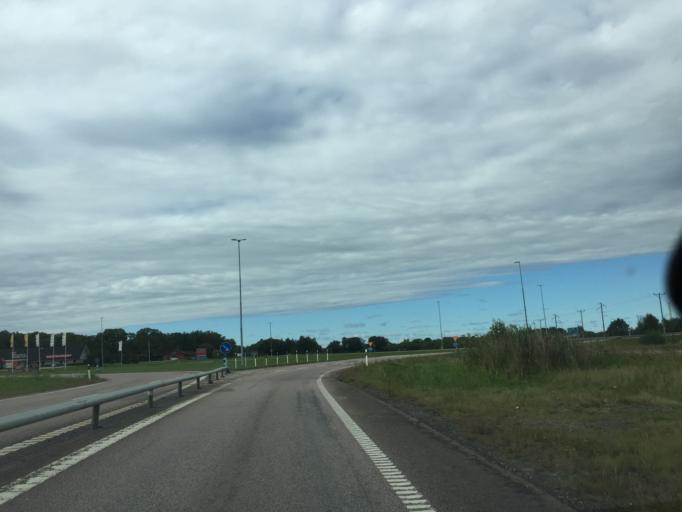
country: SE
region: Vaestmanland
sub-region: Arboga Kommun
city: Arboga
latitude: 59.3973
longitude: 15.8916
